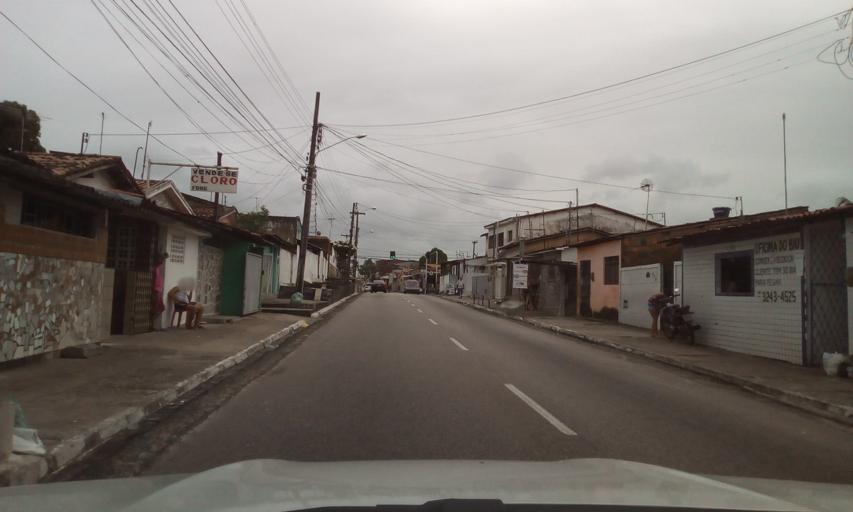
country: BR
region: Paraiba
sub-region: Joao Pessoa
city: Joao Pessoa
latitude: -7.1001
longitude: -34.8610
